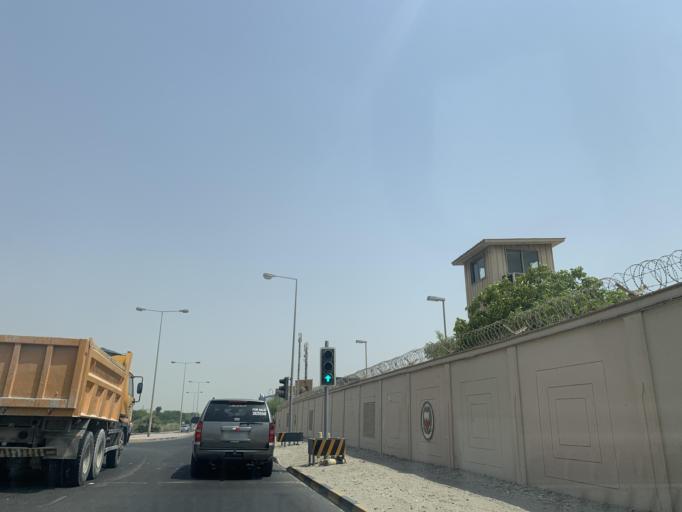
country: BH
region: Central Governorate
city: Madinat Hamad
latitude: 26.1504
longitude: 50.4856
